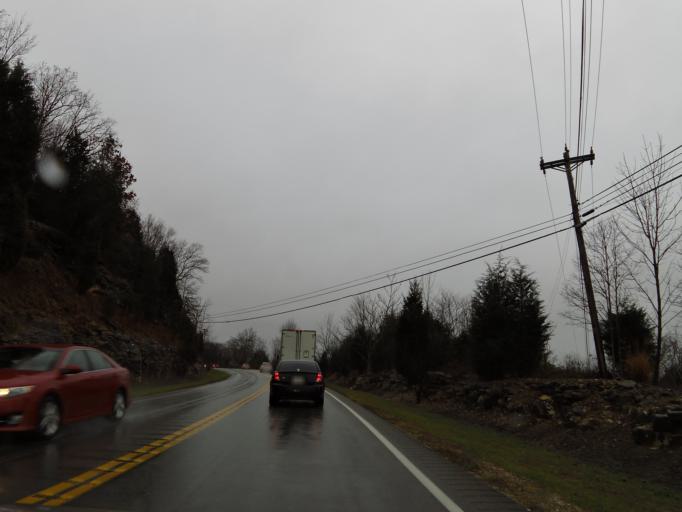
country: US
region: Kentucky
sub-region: Rockcastle County
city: Mount Vernon
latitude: 37.4118
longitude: -84.3355
